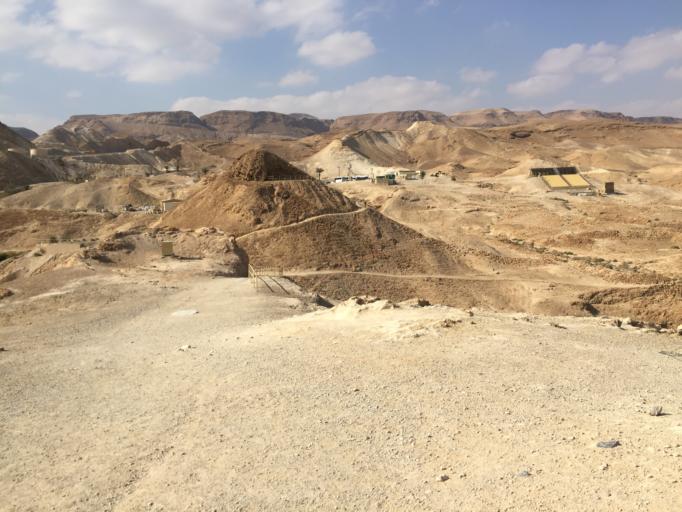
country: IL
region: Southern District
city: `En Boqeq
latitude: 31.3170
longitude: 35.3512
